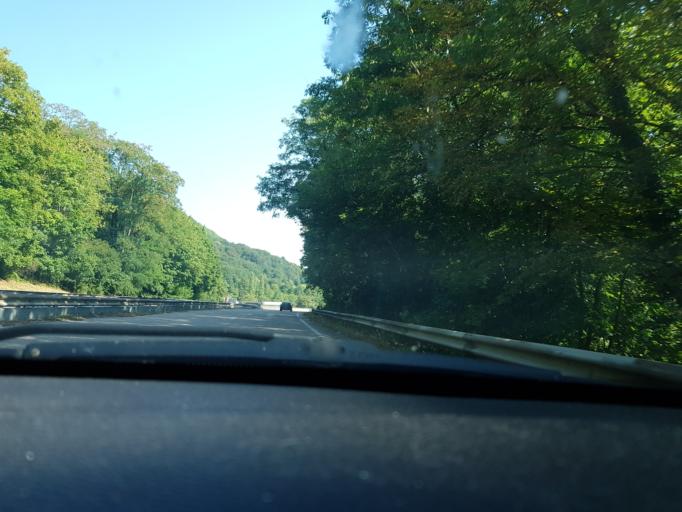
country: FR
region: Lorraine
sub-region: Departement de Meurthe-et-Moselle
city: Maxeville
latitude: 48.7104
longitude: 6.1614
